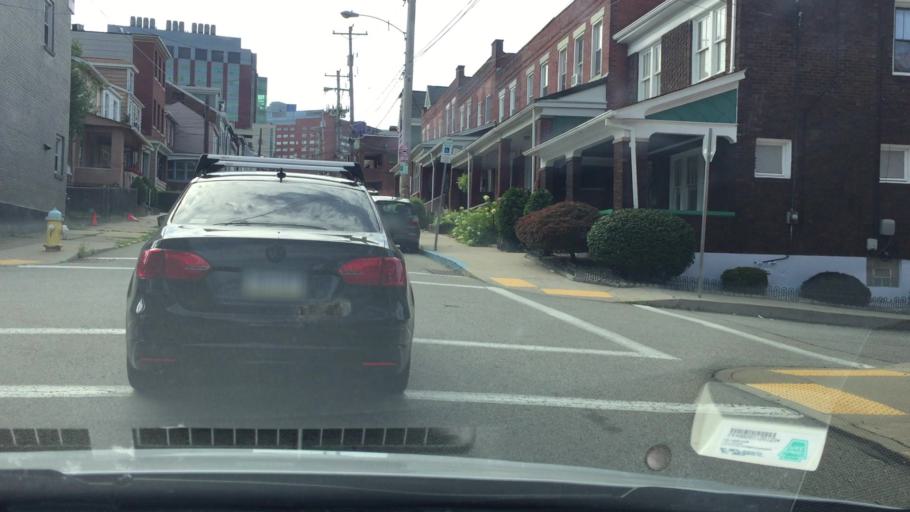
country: US
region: Pennsylvania
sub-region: Allegheny County
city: Bloomfield
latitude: 40.4701
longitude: -79.9579
